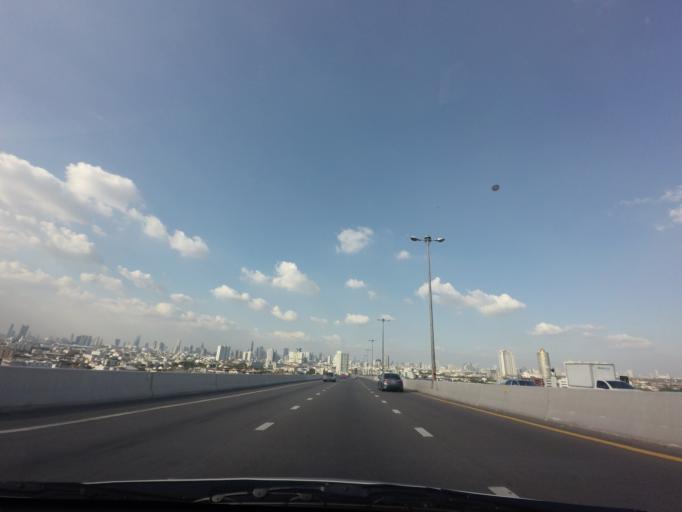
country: TH
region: Samut Prakan
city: Phra Pradaeng
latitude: 13.6728
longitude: 100.5387
